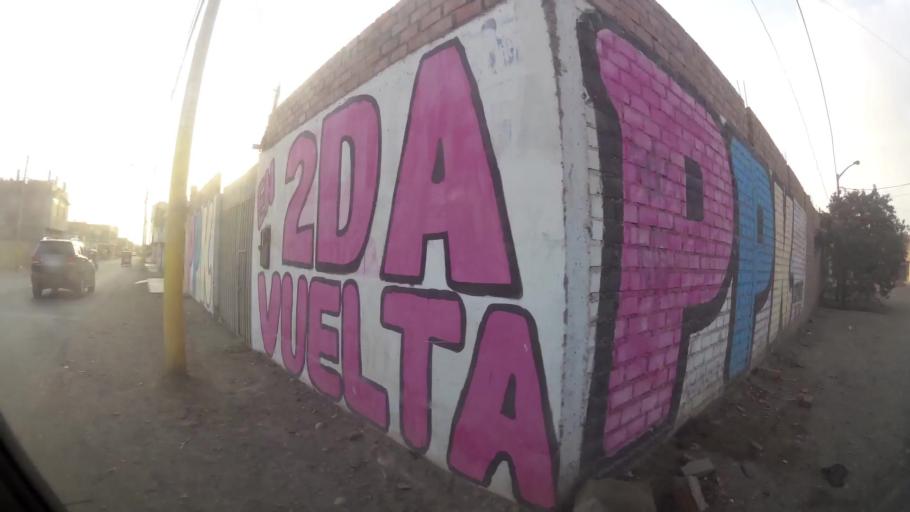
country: PE
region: Lima
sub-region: Huaura
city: Huacho
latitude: -11.1094
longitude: -77.5995
